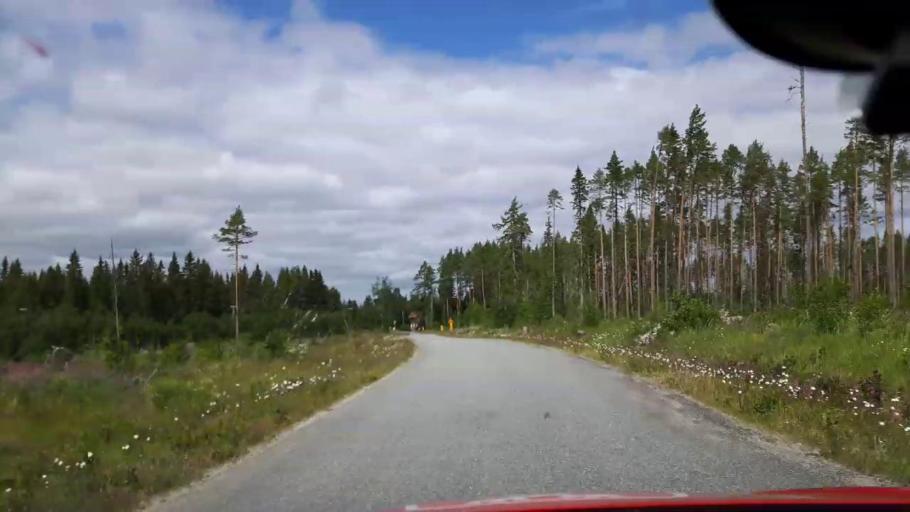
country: SE
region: Jaemtland
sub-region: Braecke Kommun
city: Braecke
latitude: 62.8376
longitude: 15.3039
